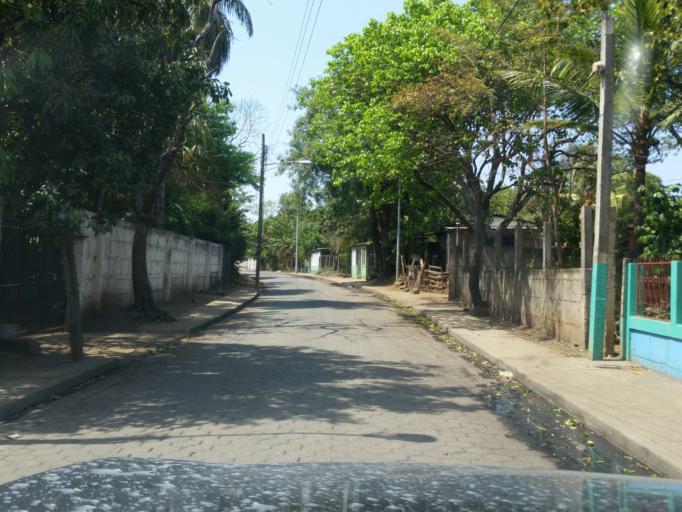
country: NI
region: Masaya
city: Ticuantepe
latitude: 12.0732
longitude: -86.2147
